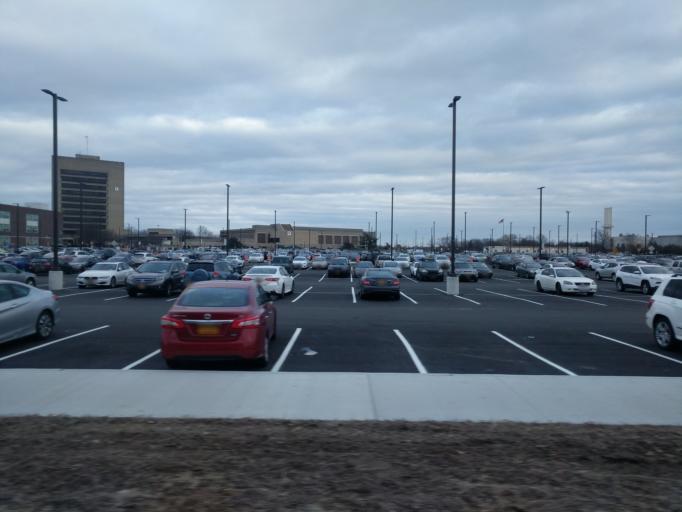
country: US
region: New York
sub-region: Nassau County
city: East Garden City
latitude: 40.7278
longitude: -73.5951
